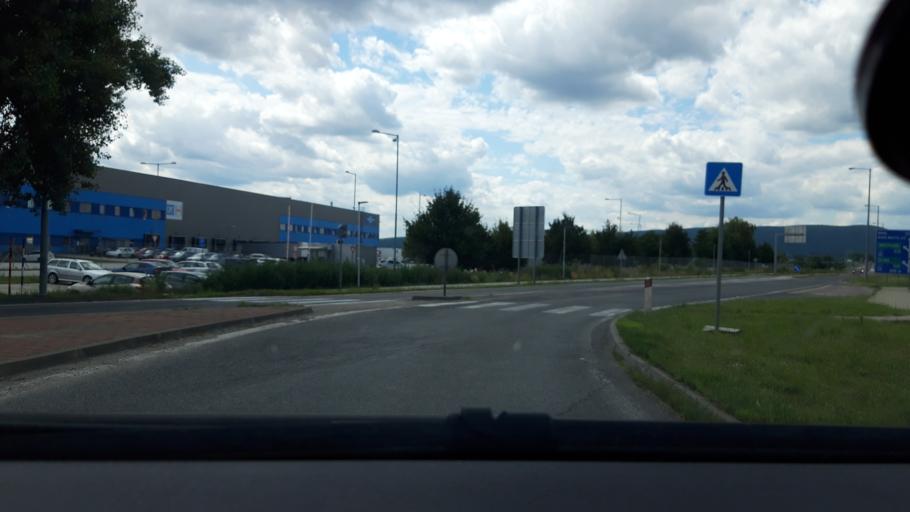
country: SK
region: Trenciansky
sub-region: Okres Nove Mesto nad Vahom
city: Nove Mesto nad Vahom
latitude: 48.7613
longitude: 17.8776
